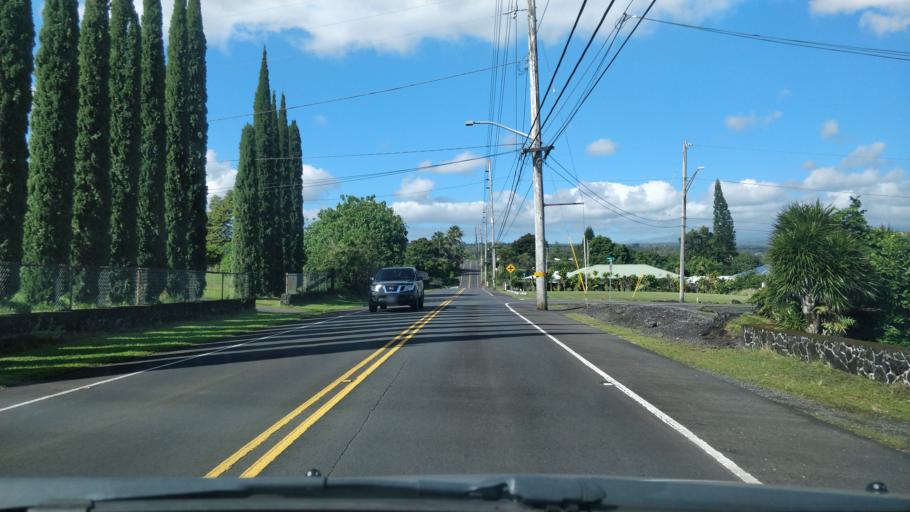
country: US
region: Hawaii
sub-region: Hawaii County
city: Hilo
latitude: 19.6824
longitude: -155.0999
